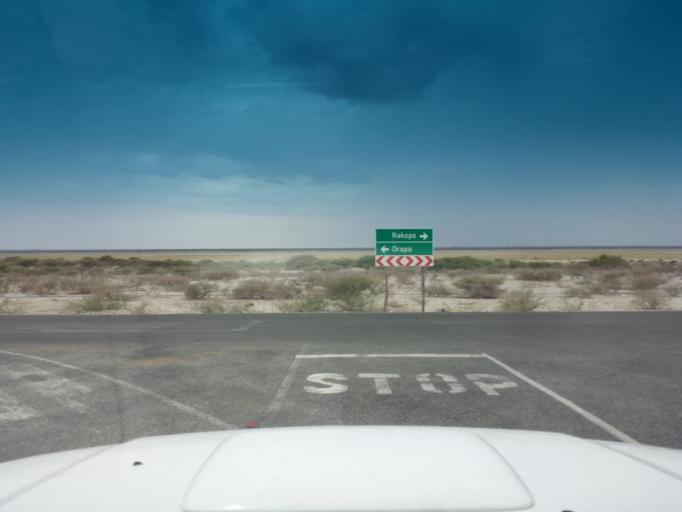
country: BW
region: Central
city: Mopipi
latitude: -21.2058
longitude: 24.8582
